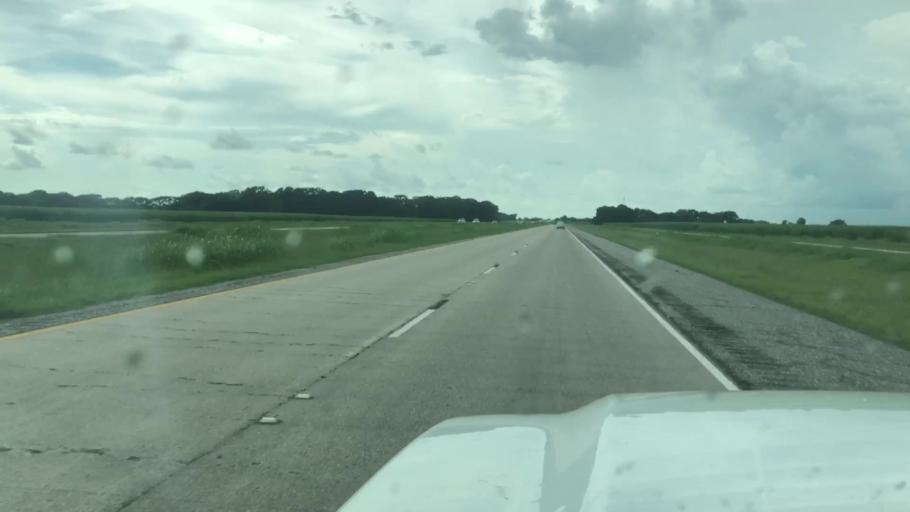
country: US
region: Louisiana
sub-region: Saint Mary Parish
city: Baldwin
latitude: 29.8536
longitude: -91.6038
